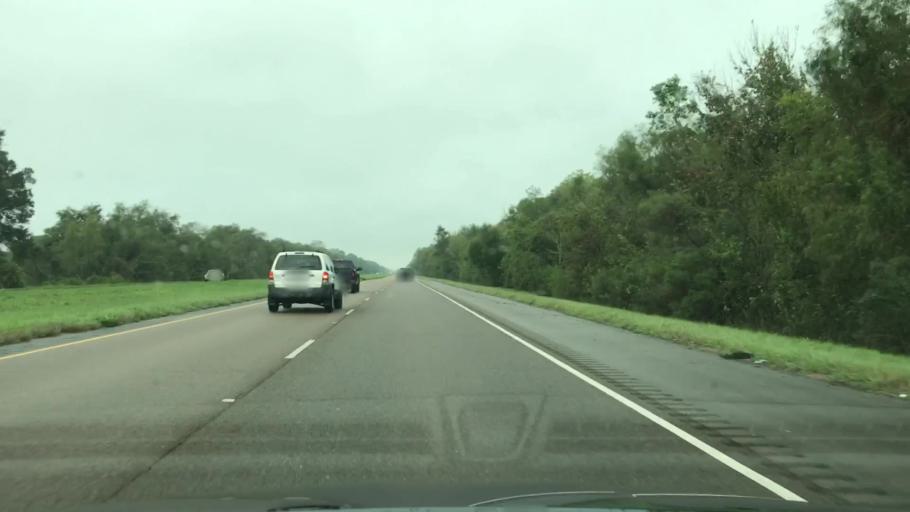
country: US
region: Louisiana
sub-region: Terrebonne Parish
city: Gray
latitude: 29.6858
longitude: -90.7176
